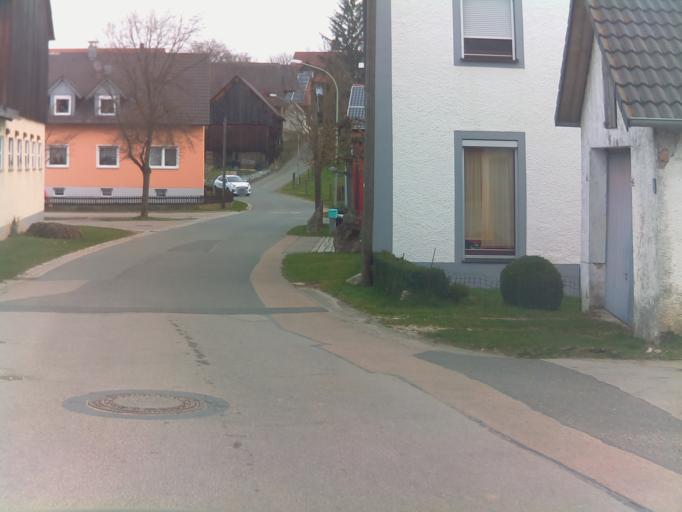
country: DE
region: Bavaria
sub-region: Upper Palatinate
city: Schmidgaden
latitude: 49.4327
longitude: 12.0536
